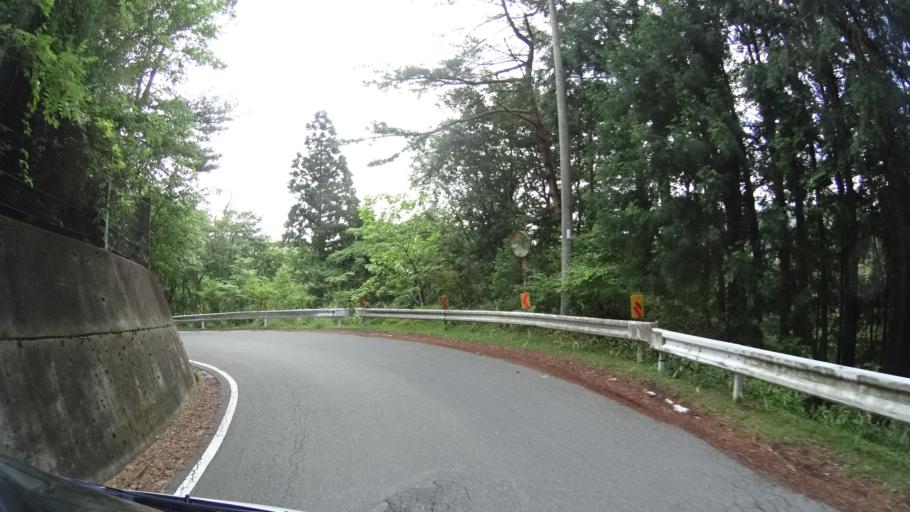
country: JP
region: Hyogo
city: Sasayama
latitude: 35.0269
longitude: 135.3869
